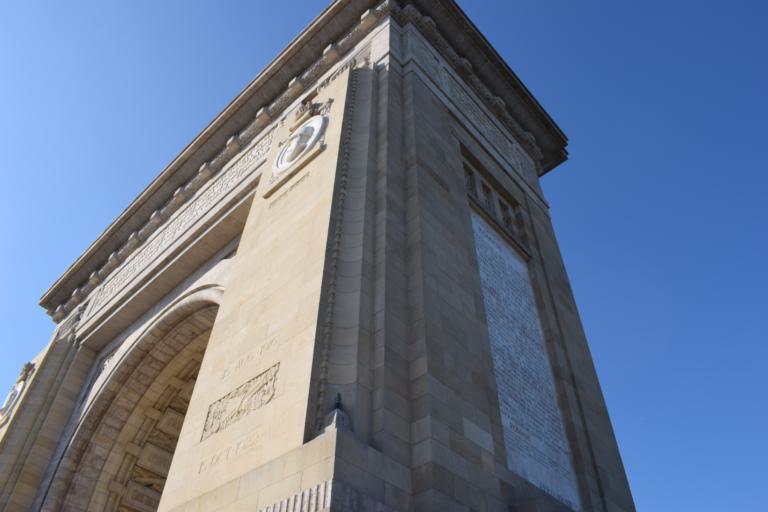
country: RO
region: Ilfov
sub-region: Comuna Popesti-Leordeni
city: Popesti-Leordeni
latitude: 44.4177
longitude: 26.1600
